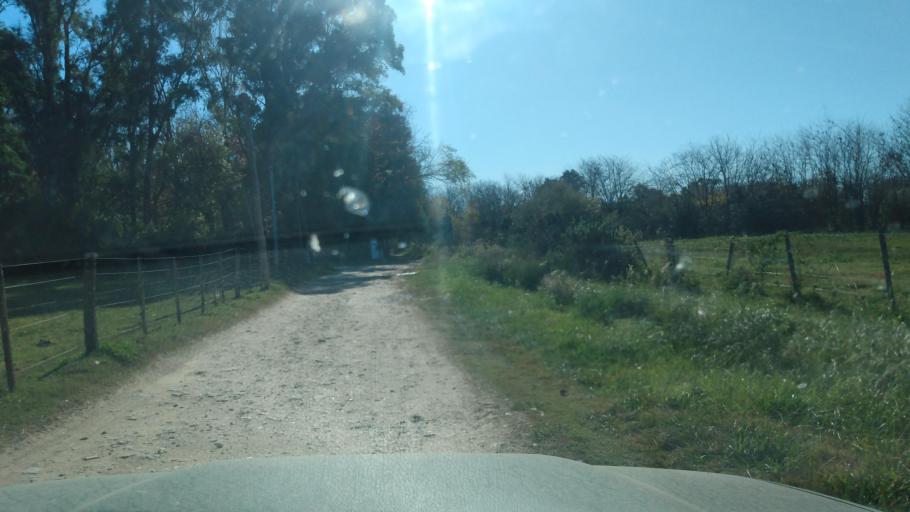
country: AR
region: Buenos Aires
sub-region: Partido de Lujan
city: Lujan
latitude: -34.4842
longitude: -59.2246
